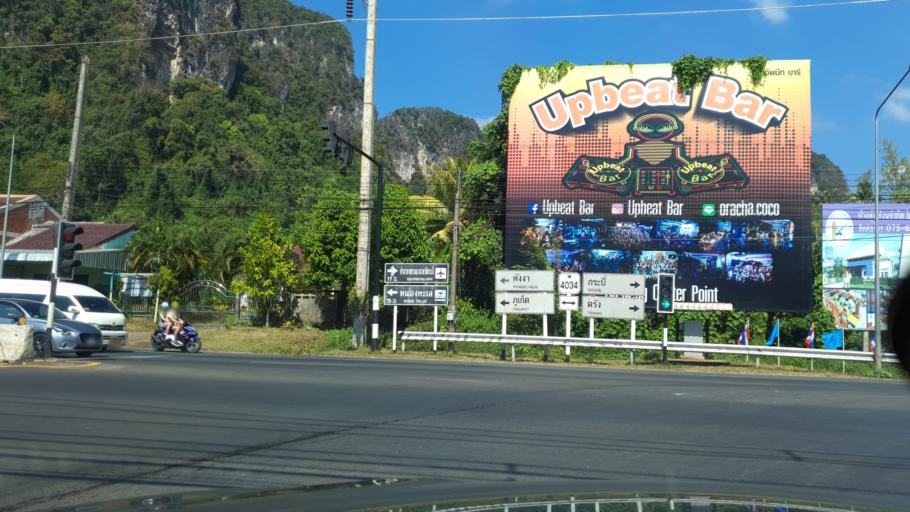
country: TH
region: Krabi
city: Krabi
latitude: 8.0796
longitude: 98.8557
